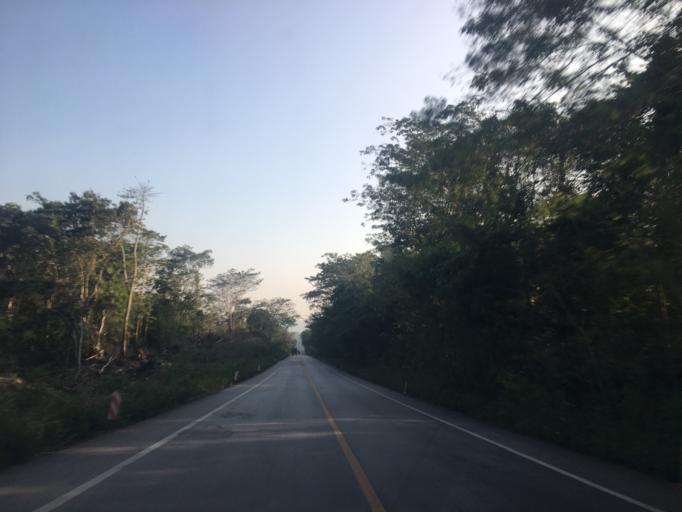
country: TH
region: Lampang
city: Ngao
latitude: 18.6577
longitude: 100.0176
